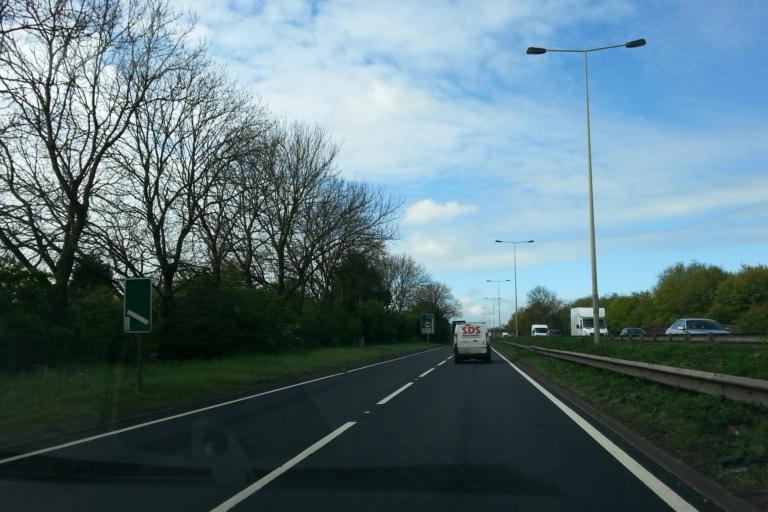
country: GB
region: England
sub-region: Staffordshire
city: Barton under Needwood
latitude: 52.7502
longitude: -1.7166
